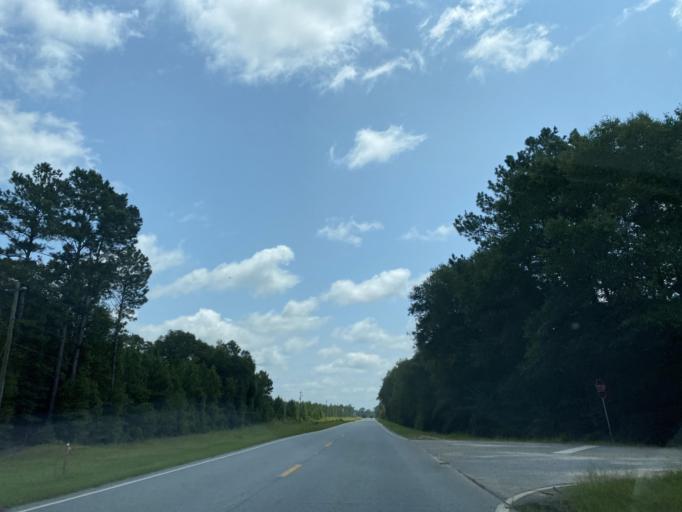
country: US
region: Georgia
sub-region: Telfair County
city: Helena
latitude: 32.0296
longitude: -83.0230
